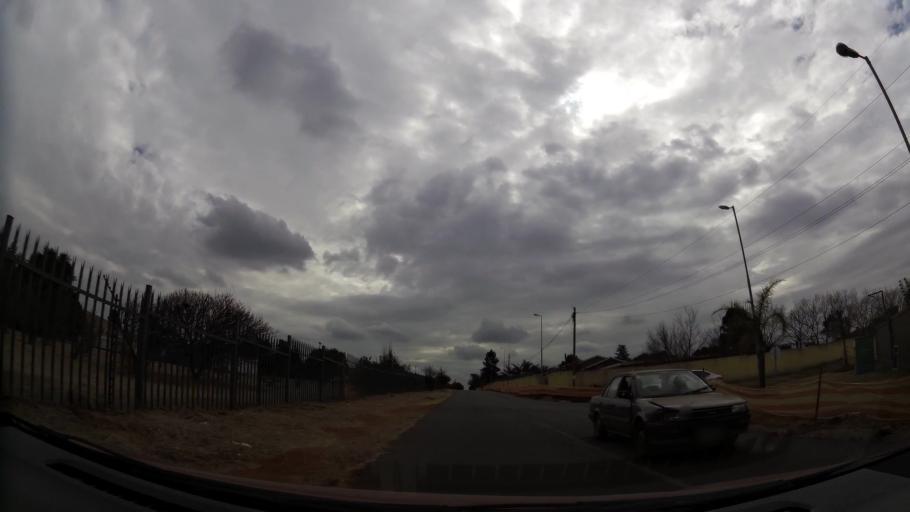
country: ZA
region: Gauteng
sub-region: West Rand District Municipality
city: Muldersdriseloop
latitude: -26.0911
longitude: 27.8751
